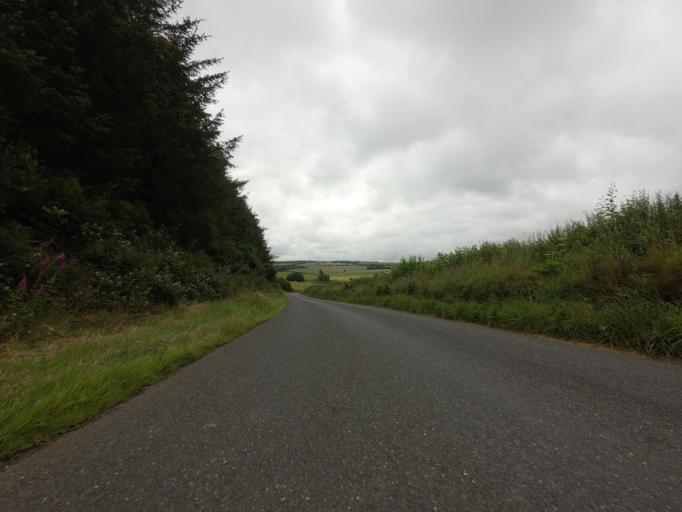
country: GB
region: Scotland
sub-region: Aberdeenshire
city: Turriff
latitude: 57.5337
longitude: -2.4026
